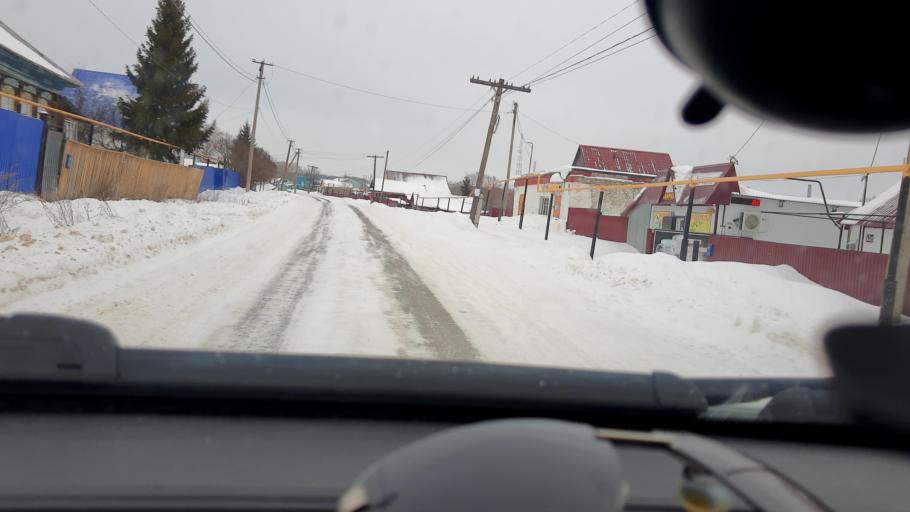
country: RU
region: Bashkortostan
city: Yazykovo
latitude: 55.0314
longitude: 56.2265
